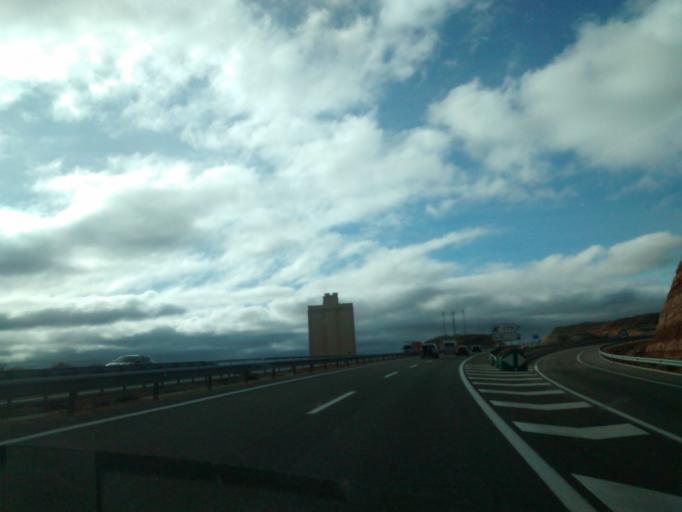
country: ES
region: Castille and Leon
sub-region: Provincia de Soria
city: Santa Maria de Huerta
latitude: 41.2711
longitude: -2.1777
